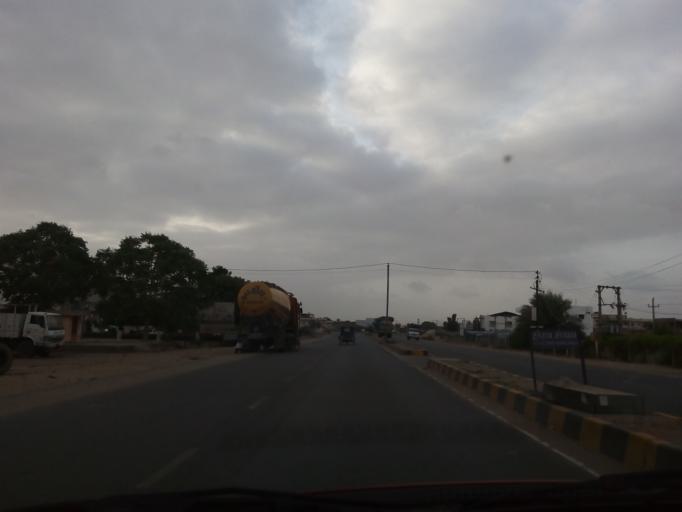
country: IN
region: Gujarat
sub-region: Kachchh
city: Bhuj
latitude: 23.2461
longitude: 69.7025
